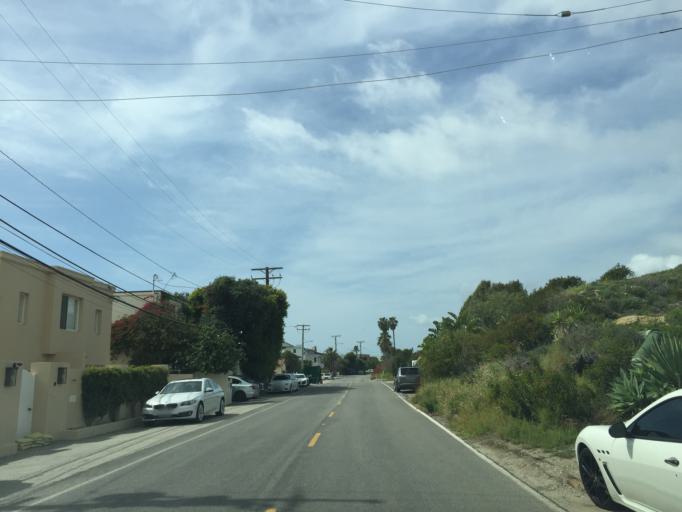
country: US
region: California
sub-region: Los Angeles County
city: Malibu Beach
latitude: 34.0306
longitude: -118.7046
